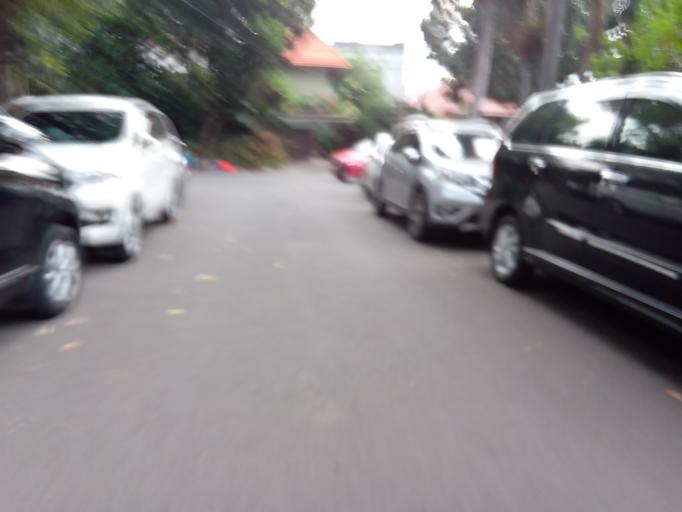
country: ID
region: Jakarta Raya
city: Jakarta
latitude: -6.1714
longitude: 106.8143
